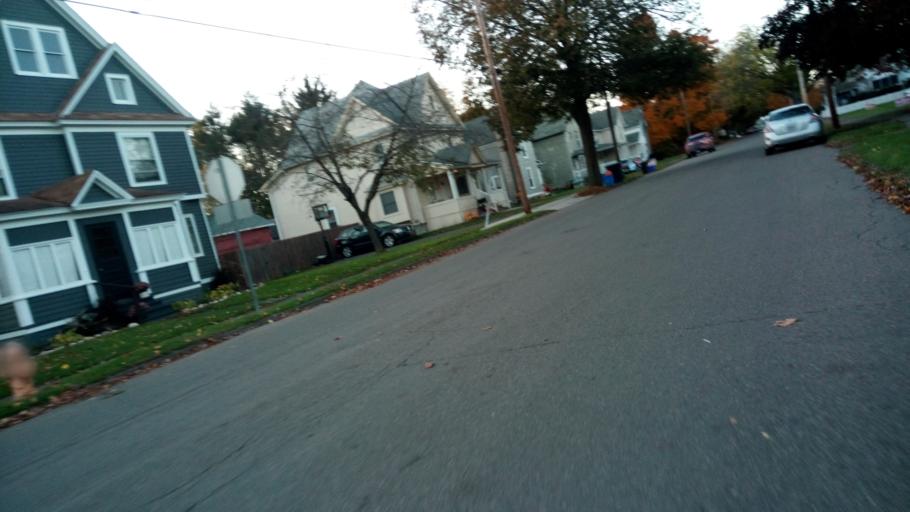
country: US
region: New York
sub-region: Chemung County
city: Southport
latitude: 42.0684
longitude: -76.8125
